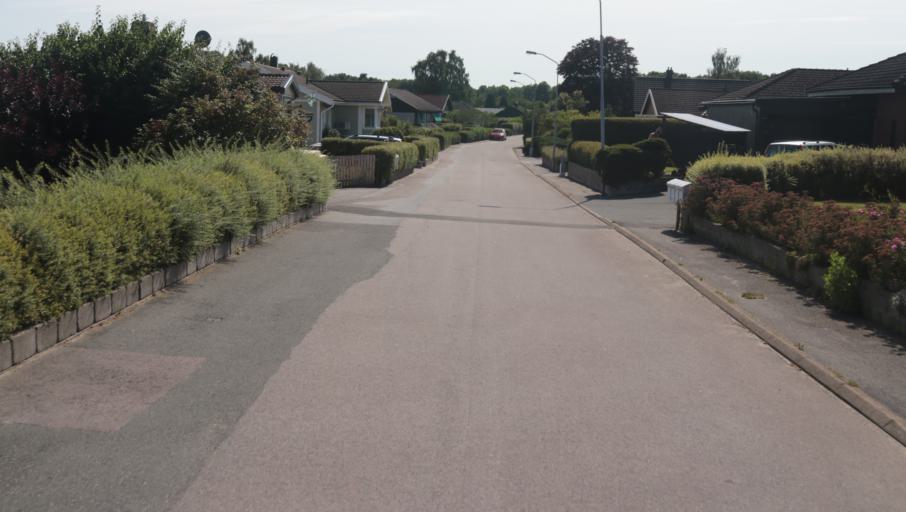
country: SE
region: Blekinge
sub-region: Karlshamns Kommun
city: Karlshamn
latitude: 56.2125
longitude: 14.8482
